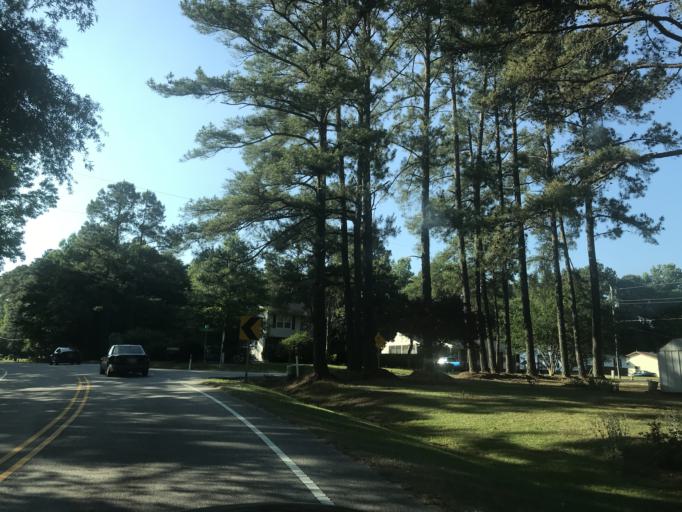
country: US
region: North Carolina
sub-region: Wake County
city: Garner
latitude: 35.7311
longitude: -78.5999
